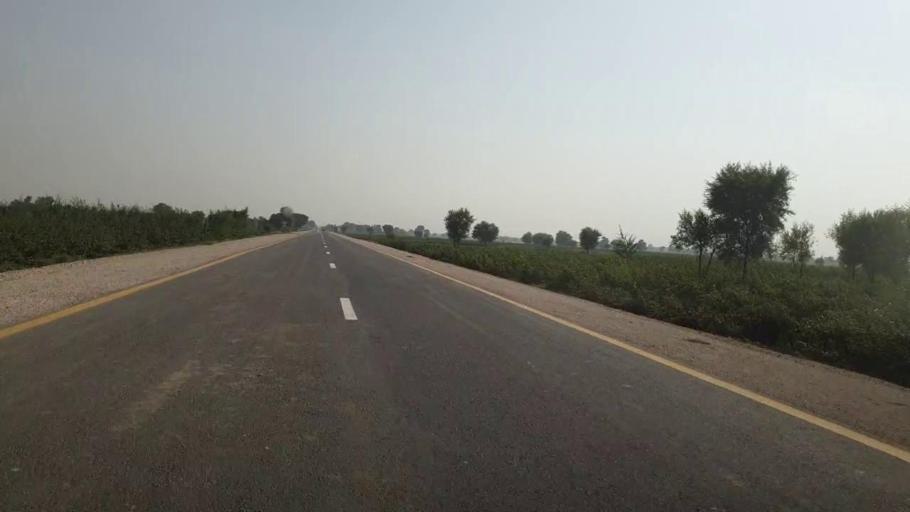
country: PK
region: Sindh
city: Bhan
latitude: 26.5446
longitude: 67.7871
